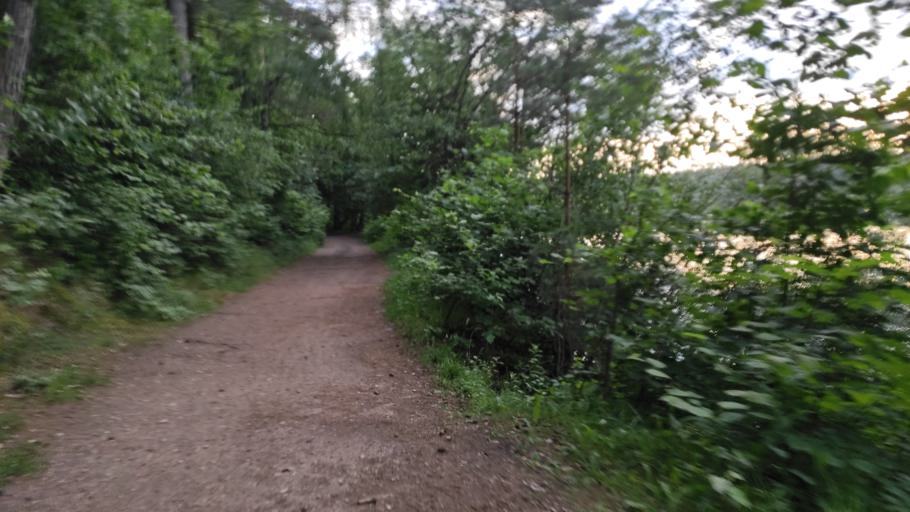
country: BY
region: Minsk
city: Zhdanovichy
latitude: 53.9634
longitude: 27.4375
